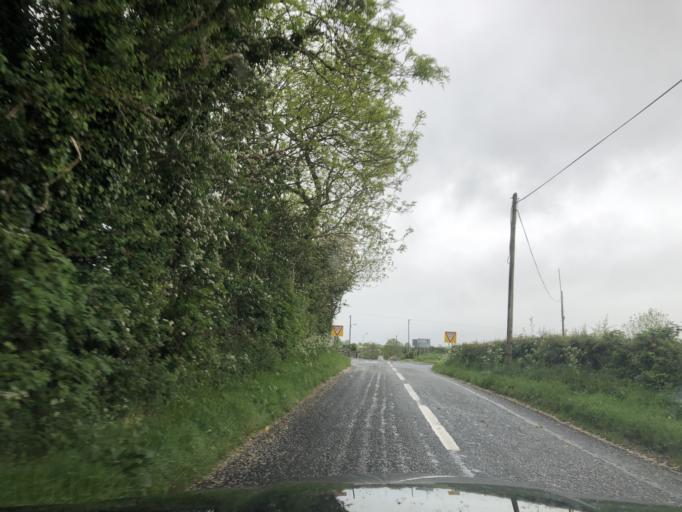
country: GB
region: Northern Ireland
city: Dunloy
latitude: 55.1225
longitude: -6.3615
